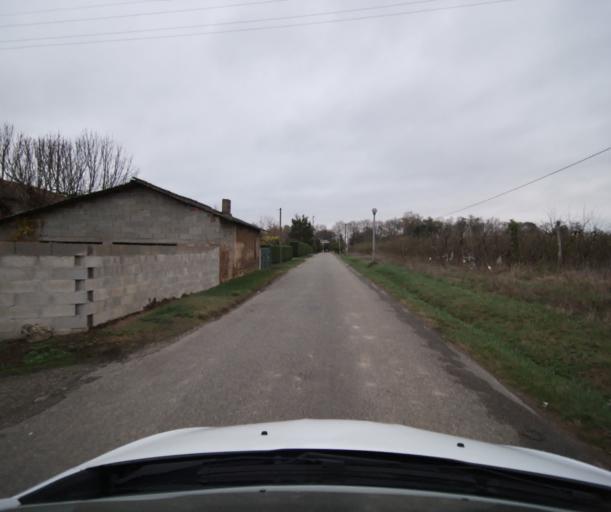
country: FR
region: Midi-Pyrenees
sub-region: Departement du Tarn-et-Garonne
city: Moissac
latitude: 44.0762
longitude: 1.0954
